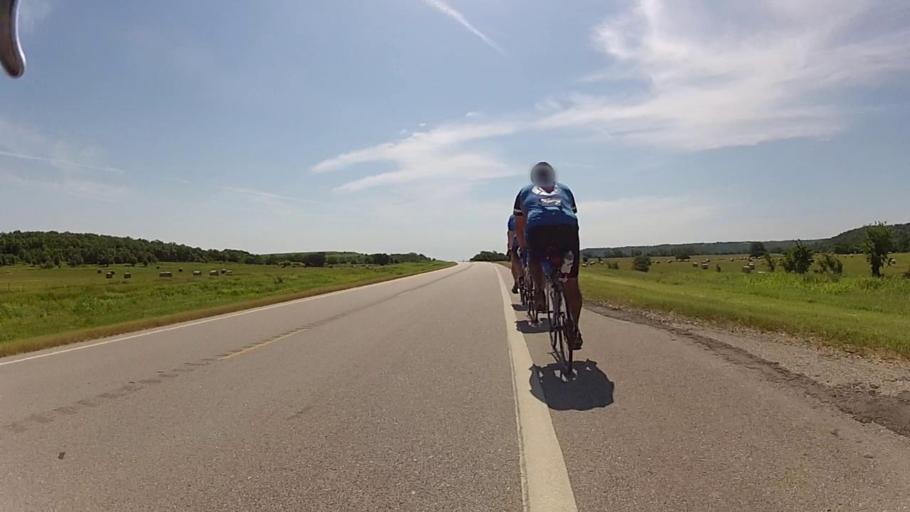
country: US
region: Kansas
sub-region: Chautauqua County
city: Sedan
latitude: 37.1078
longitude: -96.5833
